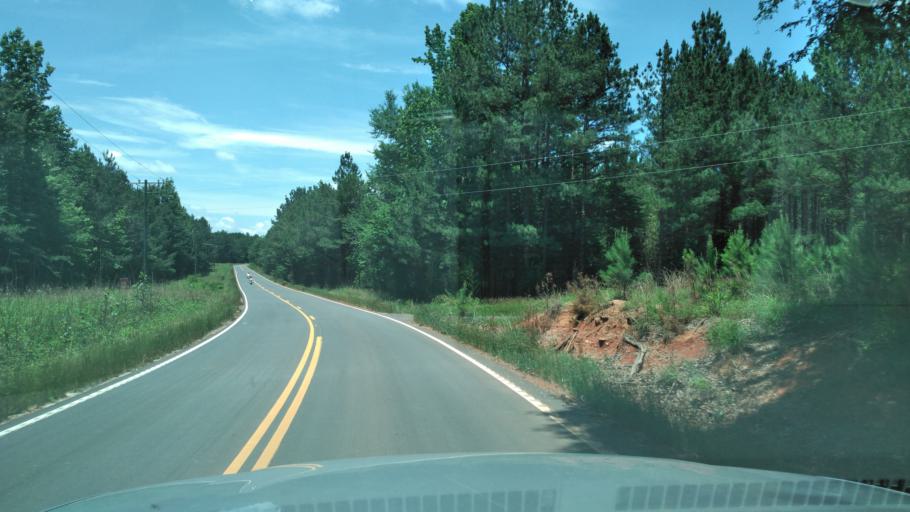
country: US
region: South Carolina
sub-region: Greenwood County
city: Ware Shoals
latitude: 34.3945
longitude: -82.1175
